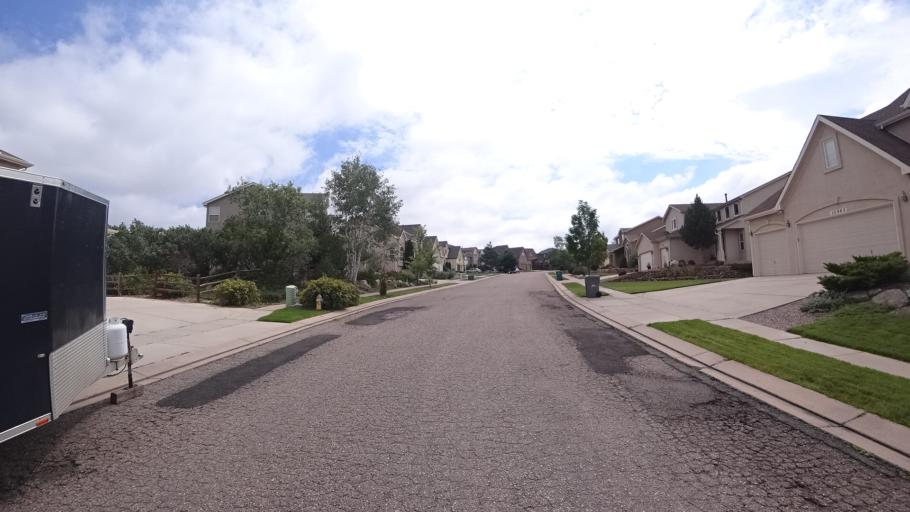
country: US
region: Colorado
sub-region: El Paso County
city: Gleneagle
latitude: 39.0165
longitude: -104.8053
